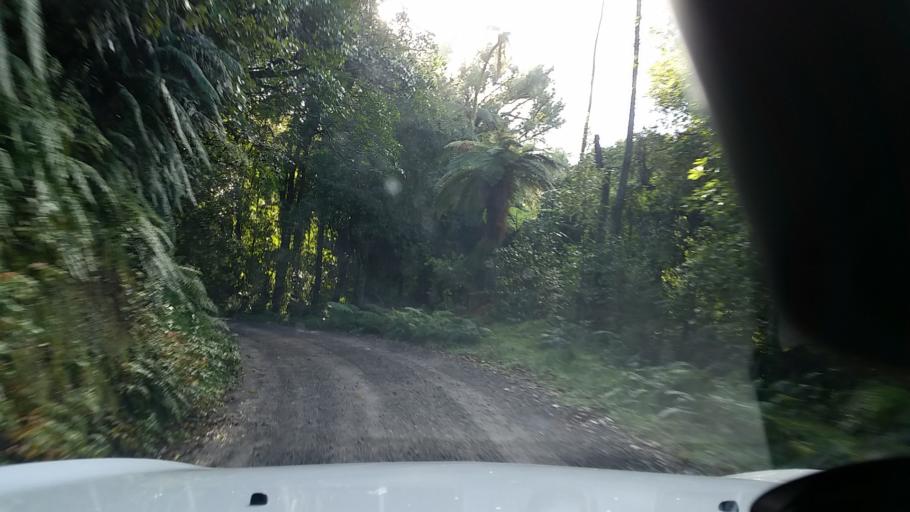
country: NZ
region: Bay of Plenty
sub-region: Kawerau District
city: Kawerau
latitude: -38.0187
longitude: 176.5890
